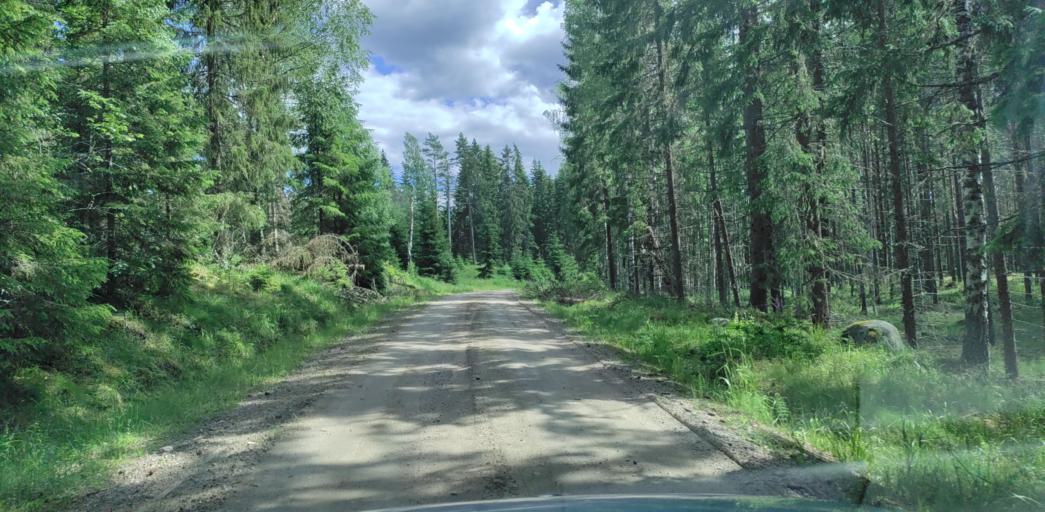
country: SE
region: Vaermland
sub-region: Hagfors Kommun
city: Ekshaerad
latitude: 60.0608
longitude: 13.3081
